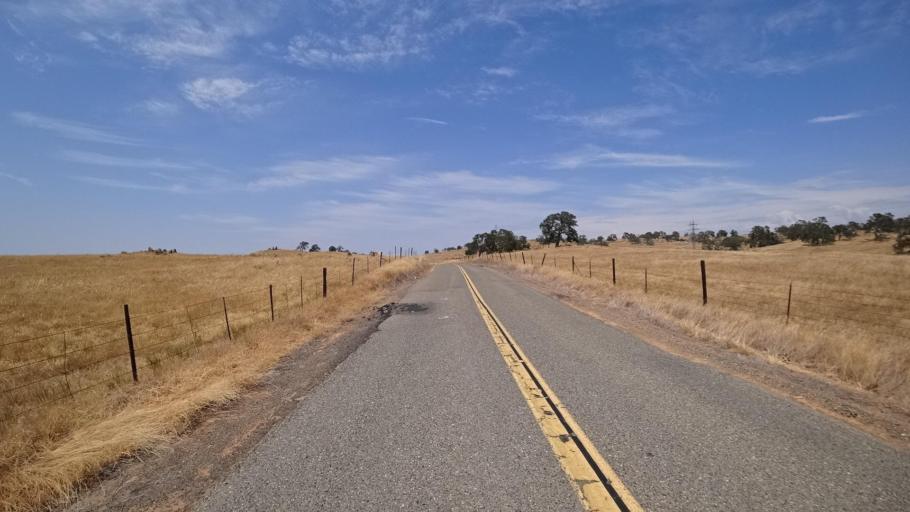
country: US
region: California
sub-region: Merced County
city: Planada
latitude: 37.5544
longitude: -120.3254
